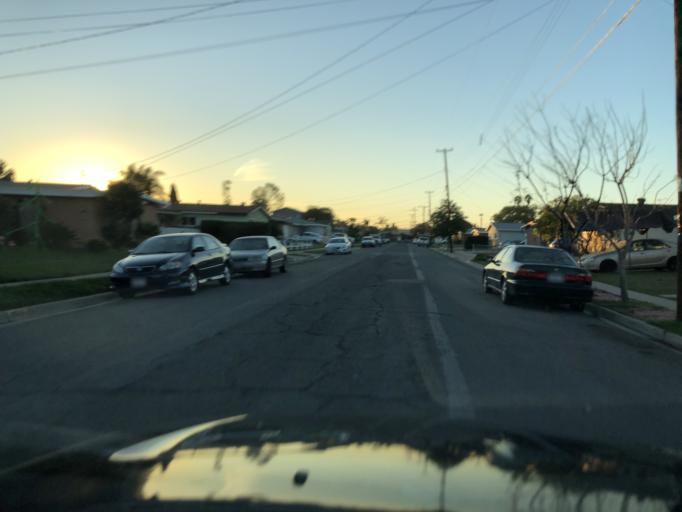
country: US
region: California
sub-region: San Diego County
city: La Jolla
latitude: 32.8366
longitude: -117.1730
